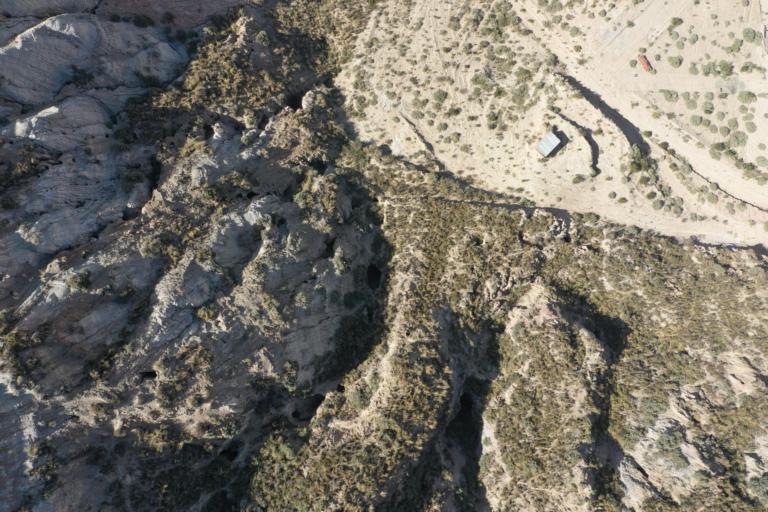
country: BO
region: La Paz
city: La Paz
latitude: -16.5524
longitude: -68.1295
